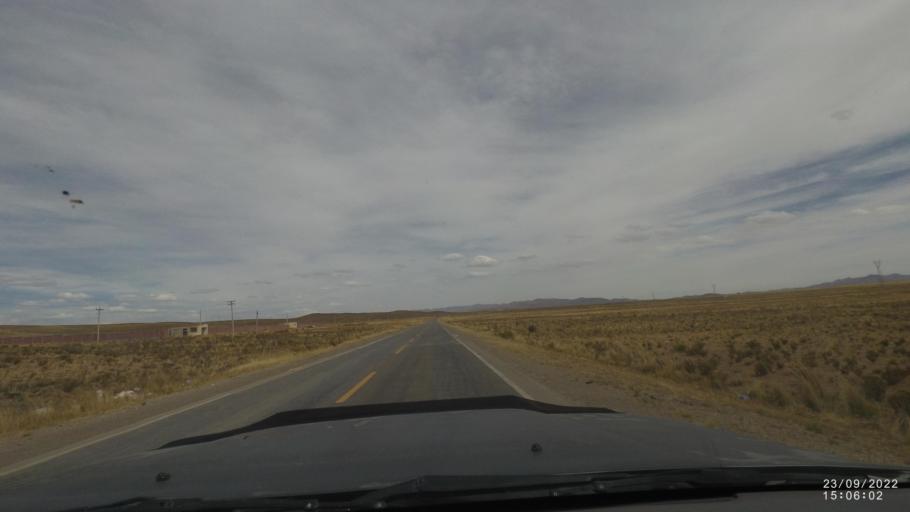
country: BO
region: Oruro
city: Oruro
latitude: -17.7360
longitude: -67.0415
